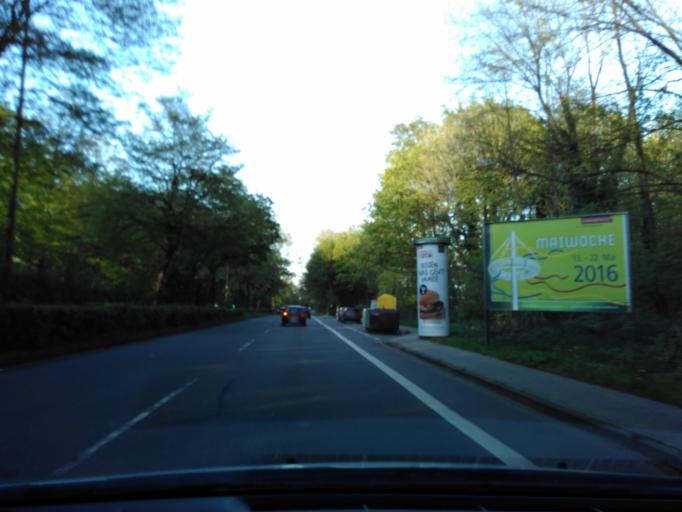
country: DE
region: Lower Saxony
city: Osnabrueck
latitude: 52.2679
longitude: 8.0129
